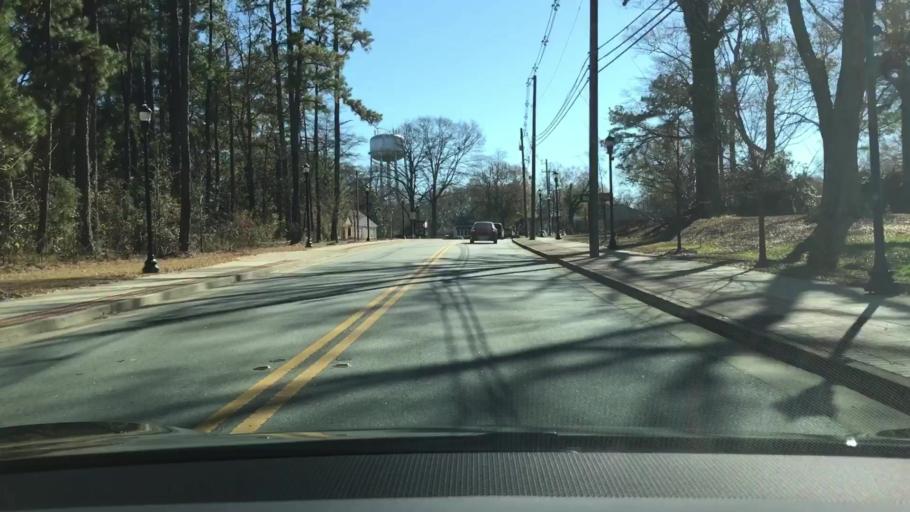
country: US
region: Georgia
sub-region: Walton County
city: Monroe
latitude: 33.7870
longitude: -83.7099
